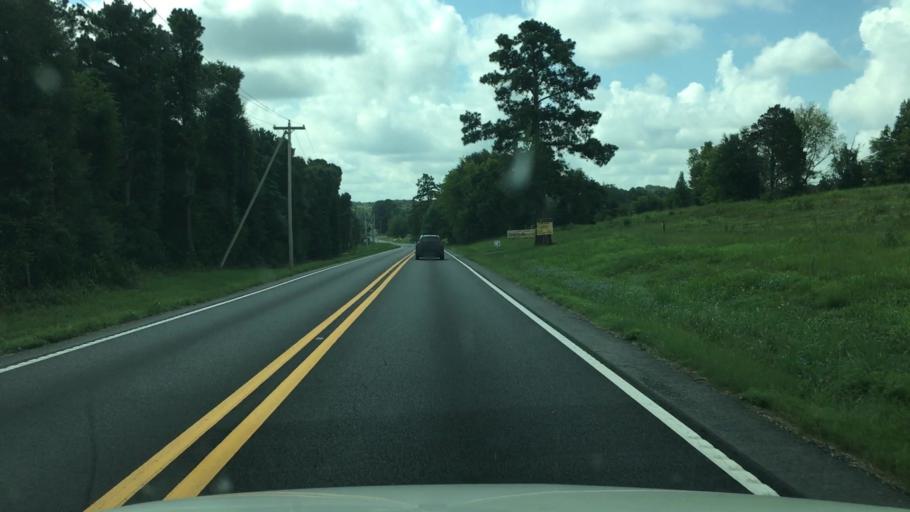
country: US
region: Arkansas
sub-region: Garland County
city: Lake Hamilton
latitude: 34.3004
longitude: -93.1645
